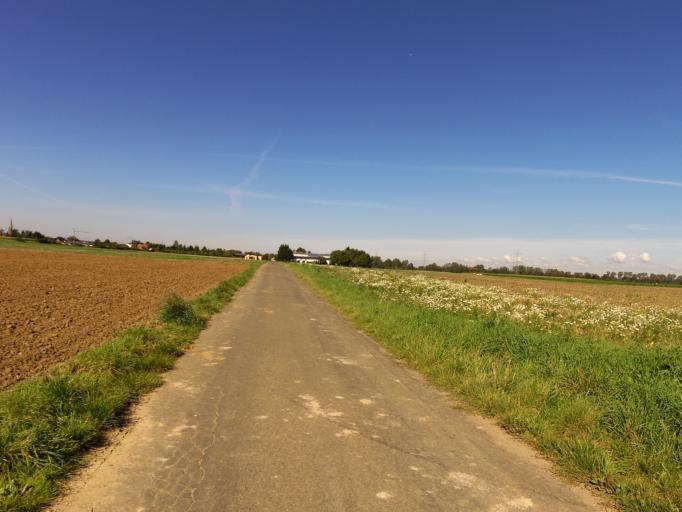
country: DE
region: North Rhine-Westphalia
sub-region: Regierungsbezirk Koln
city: Rheinbach
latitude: 50.6456
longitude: 6.8984
